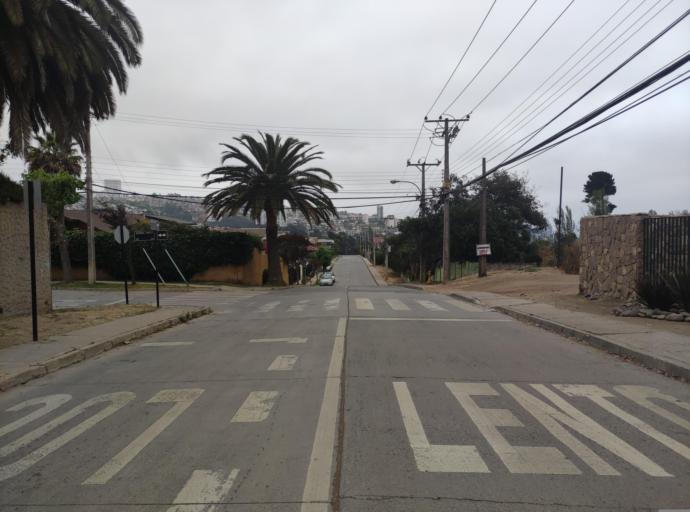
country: CL
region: Valparaiso
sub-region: Provincia de Valparaiso
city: Vina del Mar
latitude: -32.9681
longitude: -71.5265
